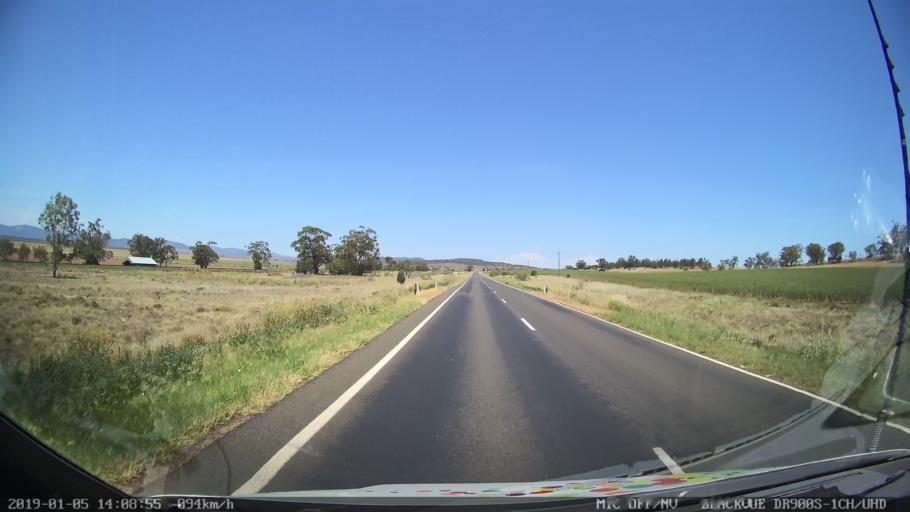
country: AU
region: New South Wales
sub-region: Gunnedah
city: Gunnedah
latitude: -31.2388
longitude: 150.4192
